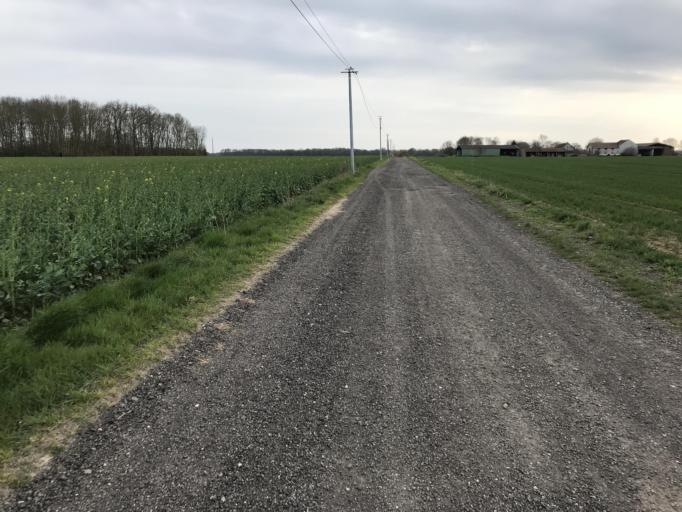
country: FR
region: Ile-de-France
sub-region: Departement de l'Essonne
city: Les Molieres
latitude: 48.6622
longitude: 2.0503
